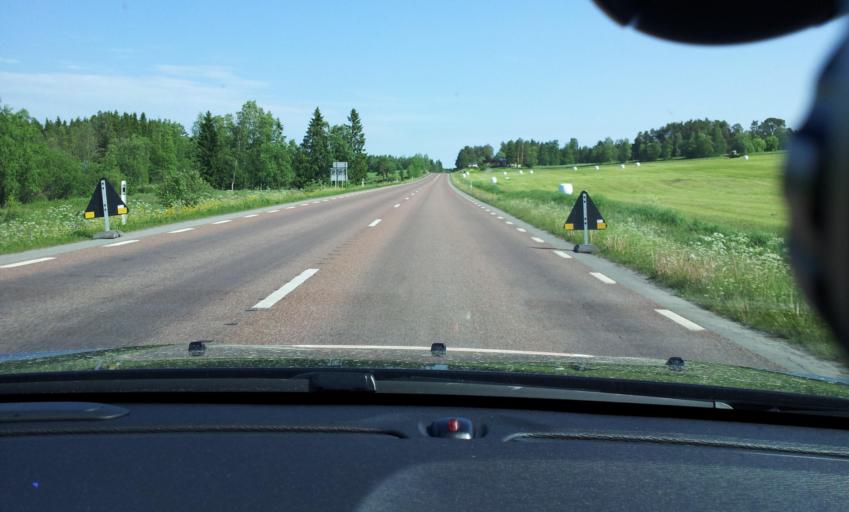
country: SE
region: Jaemtland
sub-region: Bergs Kommun
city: Hoverberg
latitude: 62.9721
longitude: 14.5608
